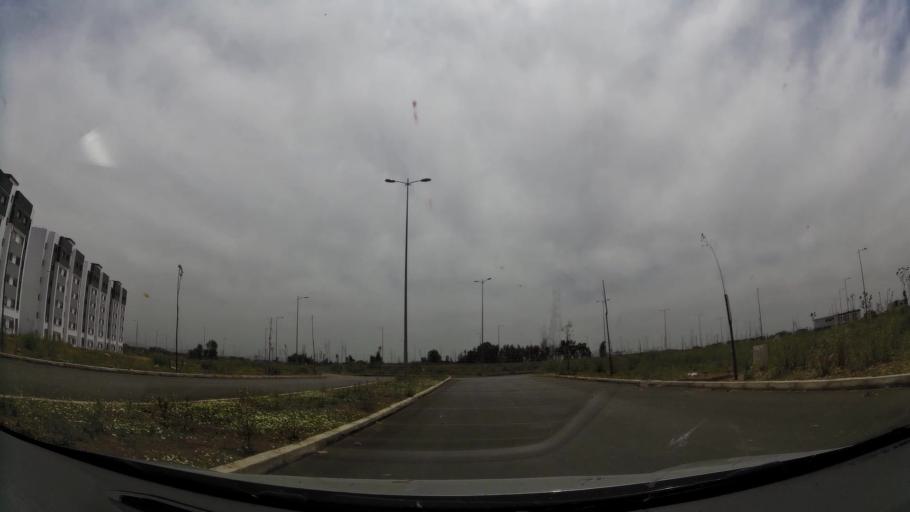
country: MA
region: Rabat-Sale-Zemmour-Zaer
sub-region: Khemisset
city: Khemisset
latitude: 33.8177
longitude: -6.0849
